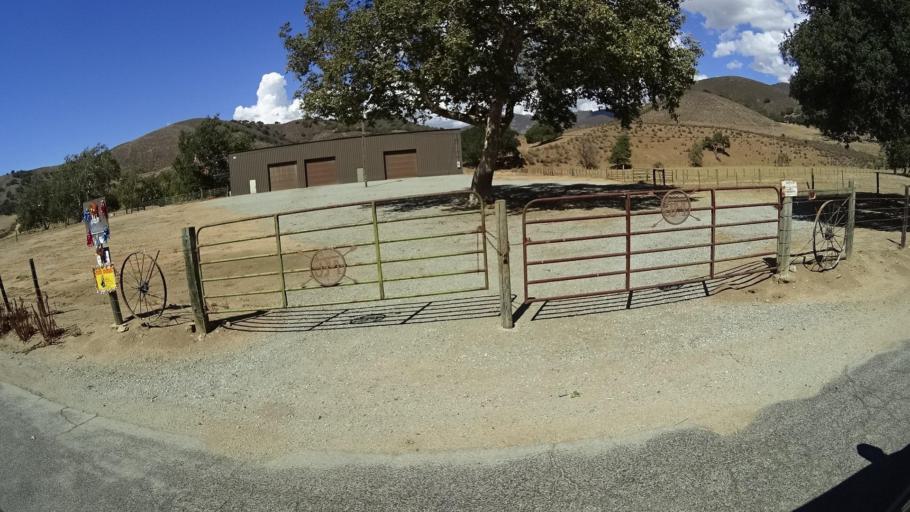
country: US
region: California
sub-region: Monterey County
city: Gonzales
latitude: 36.6030
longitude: -121.4249
